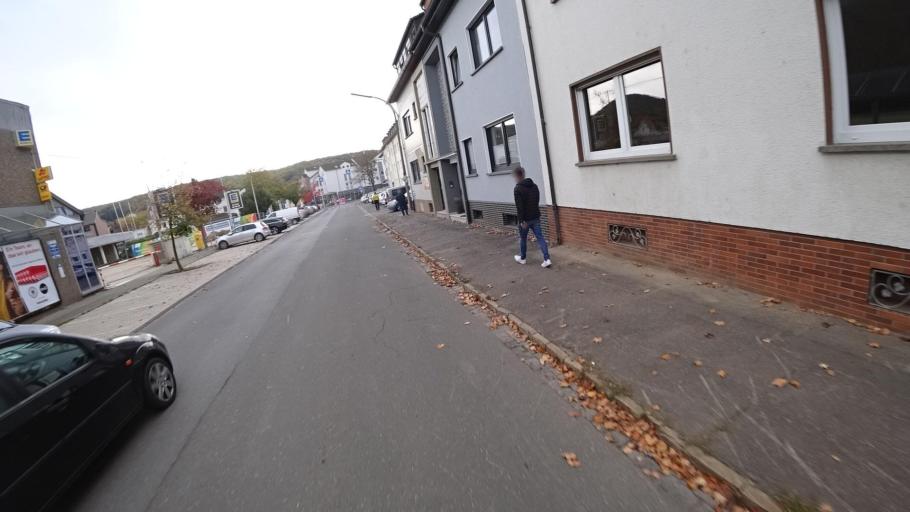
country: DE
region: Rheinland-Pfalz
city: Bad Neuenahr-Ahrweiler
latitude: 50.5460
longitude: 7.1251
